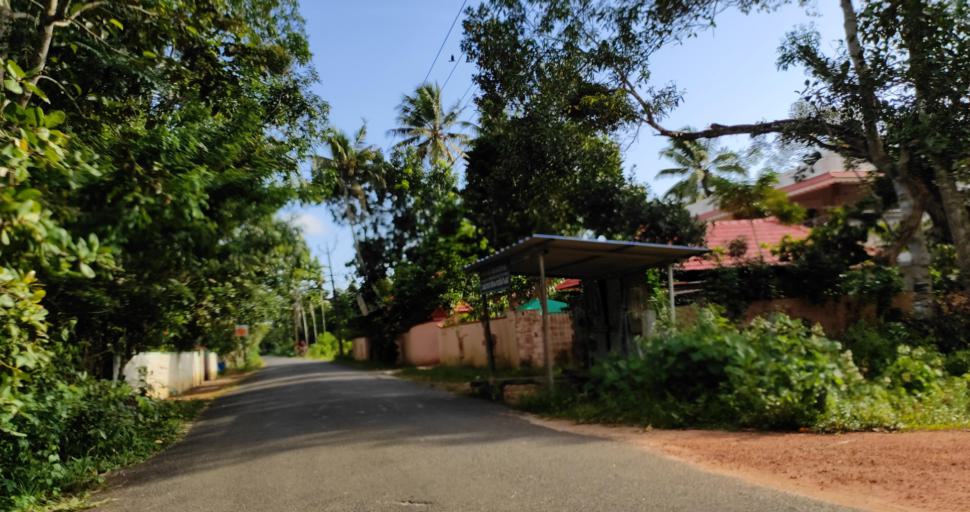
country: IN
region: Kerala
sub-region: Alappuzha
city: Shertallai
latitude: 9.6182
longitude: 76.3414
